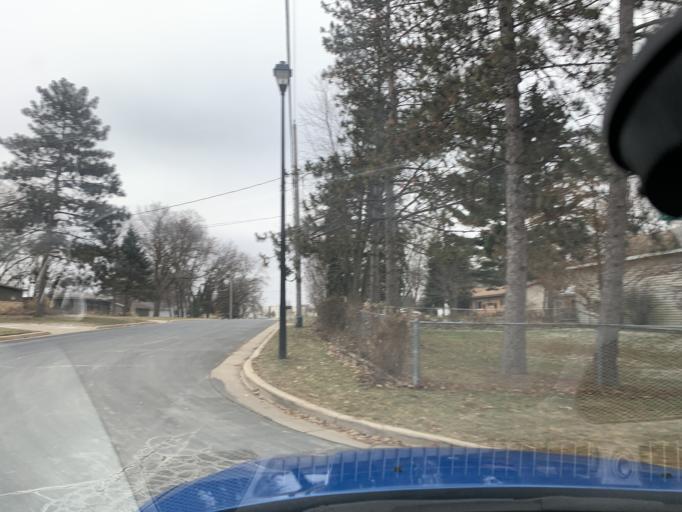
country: US
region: Wisconsin
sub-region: Dane County
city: Sun Prairie
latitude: 43.1898
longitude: -89.2383
